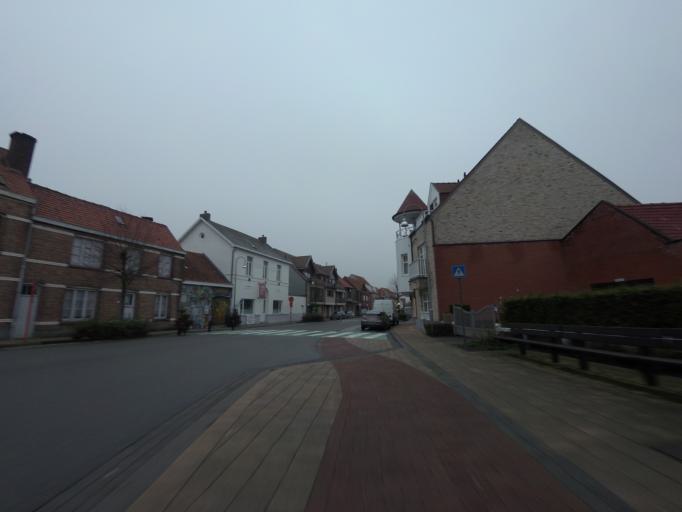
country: BE
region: Flanders
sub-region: Provincie West-Vlaanderen
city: Knokke-Heist
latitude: 51.3158
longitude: 3.3029
